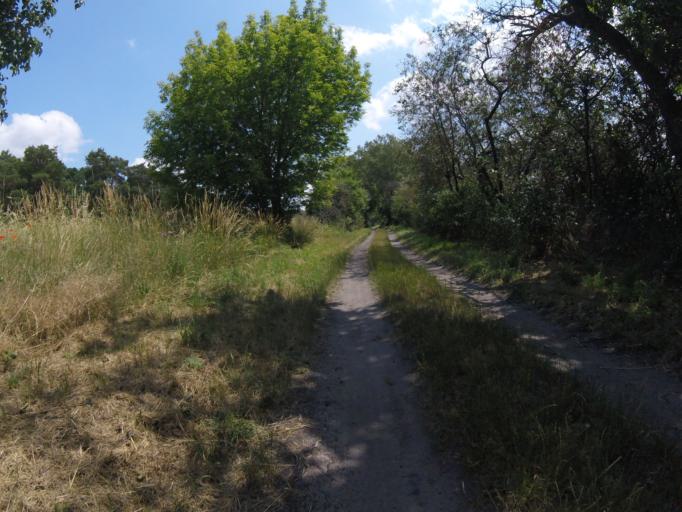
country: DE
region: Brandenburg
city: Bestensee
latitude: 52.2658
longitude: 13.7061
